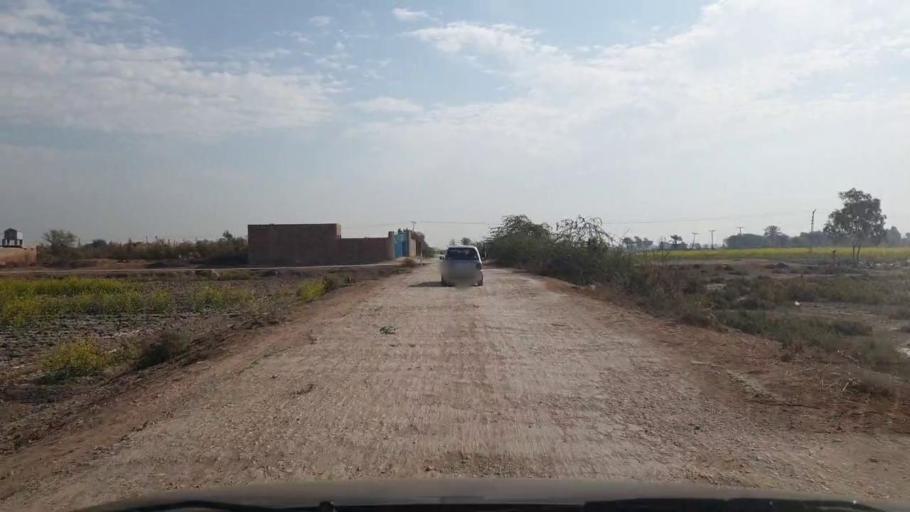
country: PK
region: Sindh
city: Sakrand
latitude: 26.0020
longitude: 68.4008
